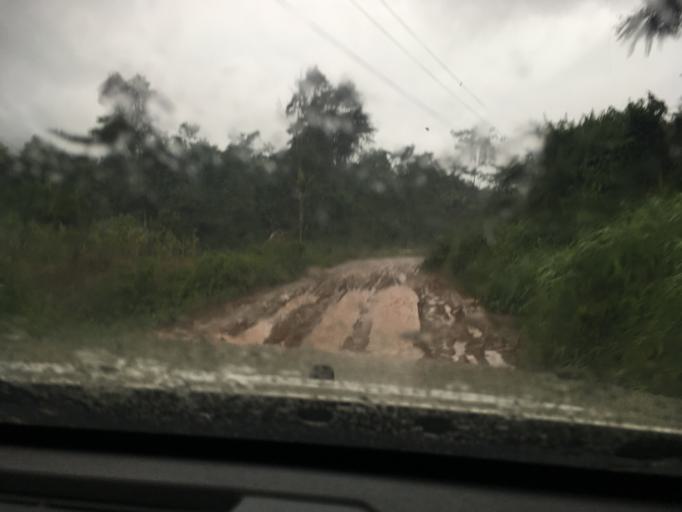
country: LA
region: Oudomxai
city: Muang La
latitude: 21.2252
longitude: 101.9718
